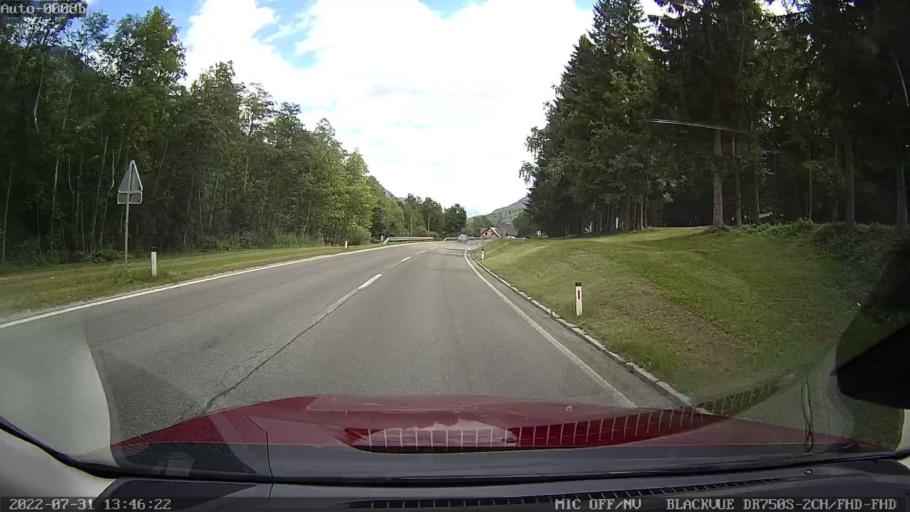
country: SI
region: Kranjska Gora
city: Kranjska Gora
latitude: 46.4896
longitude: 13.7718
